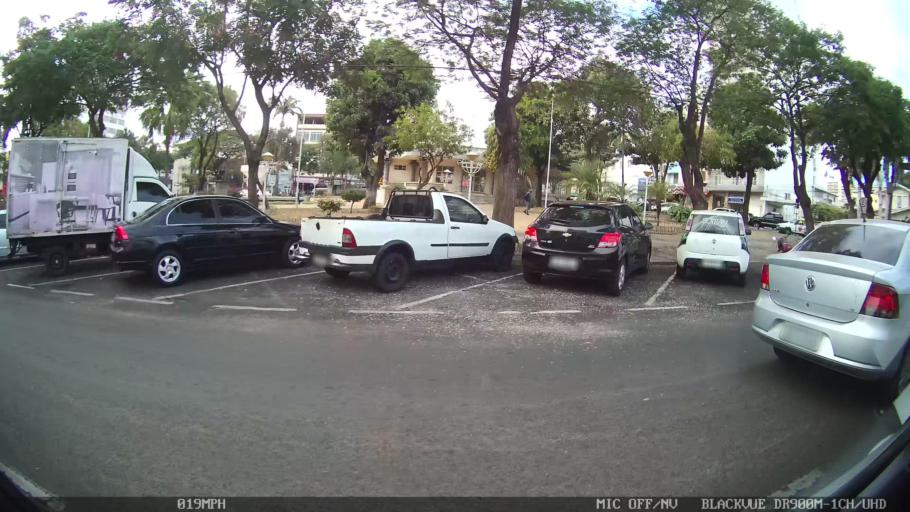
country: BR
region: Sao Paulo
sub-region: Catanduva
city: Catanduva
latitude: -21.1354
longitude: -48.9731
